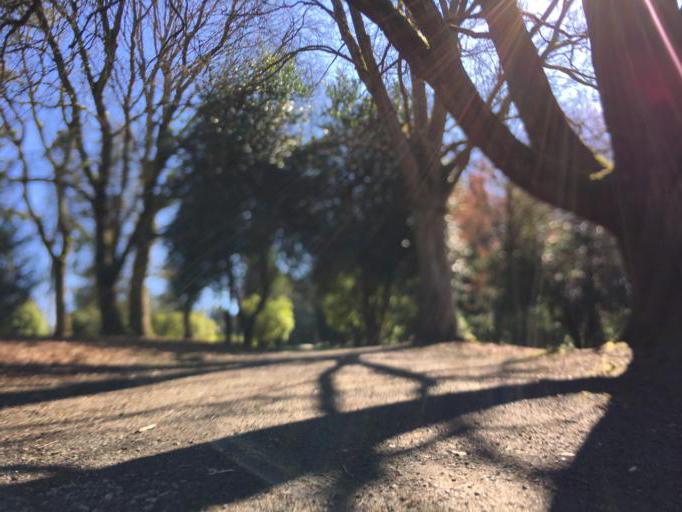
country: US
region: Washington
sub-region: King County
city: Seattle
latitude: 47.6312
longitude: -122.3181
